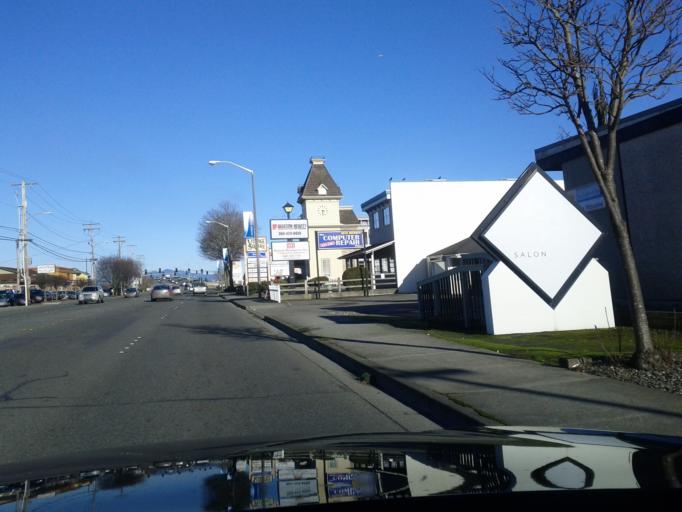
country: US
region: Washington
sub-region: Skagit County
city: Mount Vernon
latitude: 48.4395
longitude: -122.3351
